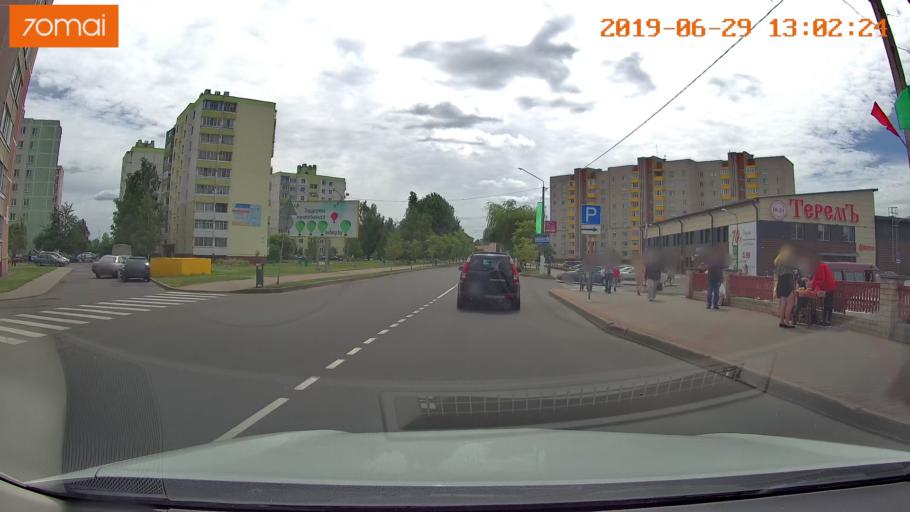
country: BY
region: Minsk
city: Slutsk
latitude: 53.0351
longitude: 27.5599
